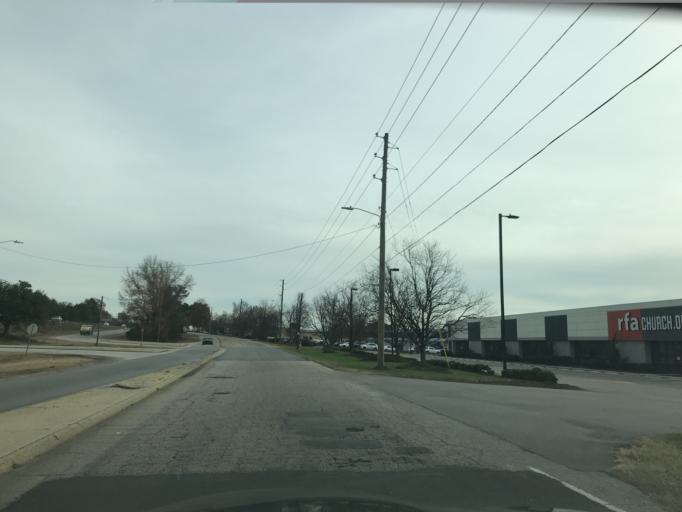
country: US
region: North Carolina
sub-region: Wake County
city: Raleigh
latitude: 35.8054
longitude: -78.5977
